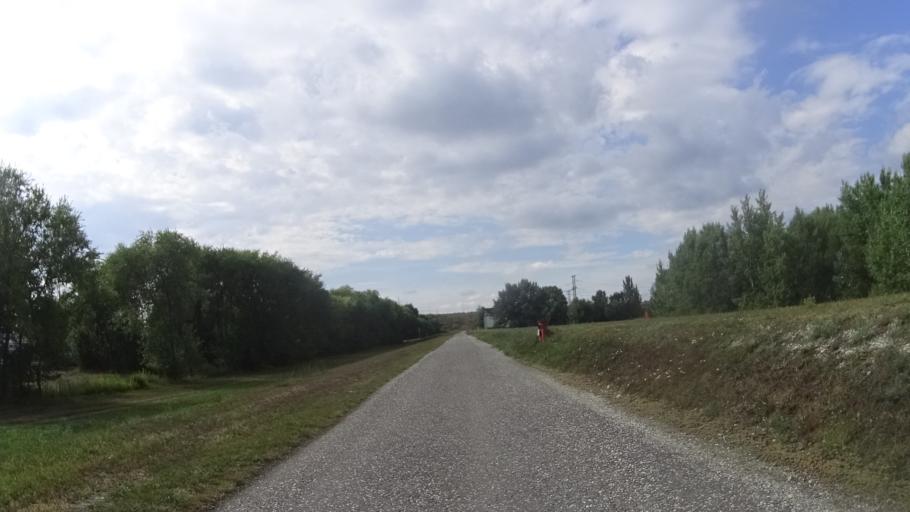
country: SK
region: Trnavsky
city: Gabcikovo
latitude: 47.8800
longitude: 17.5467
